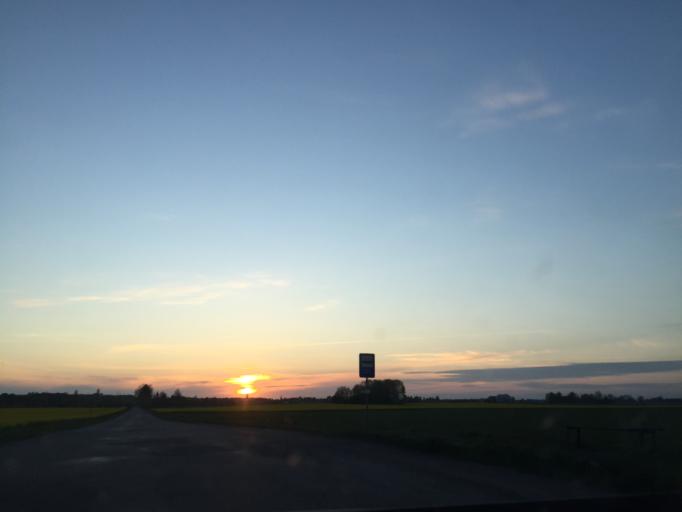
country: LV
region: Rundales
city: Pilsrundale
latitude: 56.4321
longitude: 24.0786
